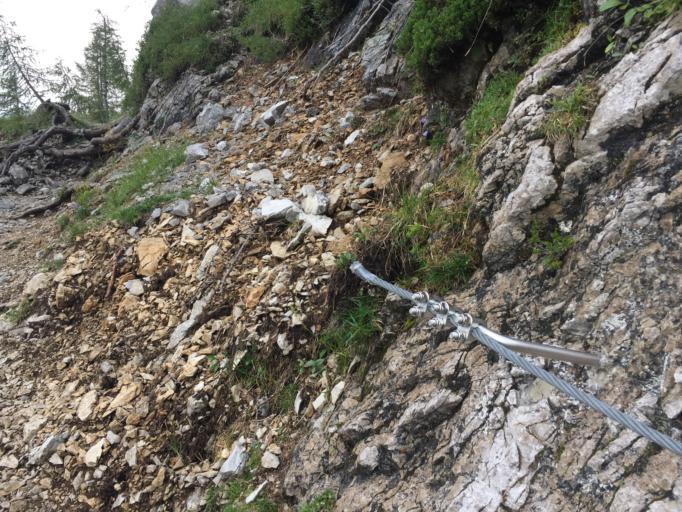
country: IT
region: Veneto
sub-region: Provincia di Belluno
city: Granvilla
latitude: 46.5507
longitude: 12.7327
